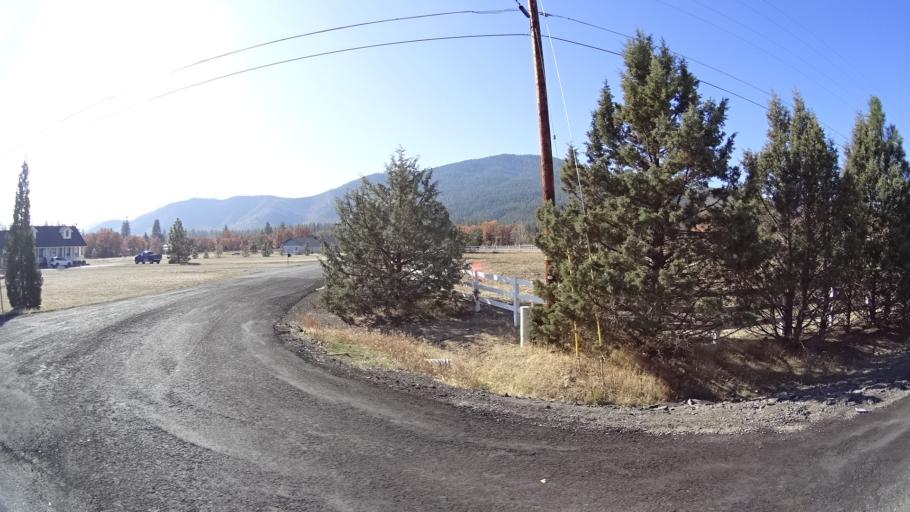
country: US
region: California
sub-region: Siskiyou County
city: Yreka
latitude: 41.6600
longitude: -122.5952
